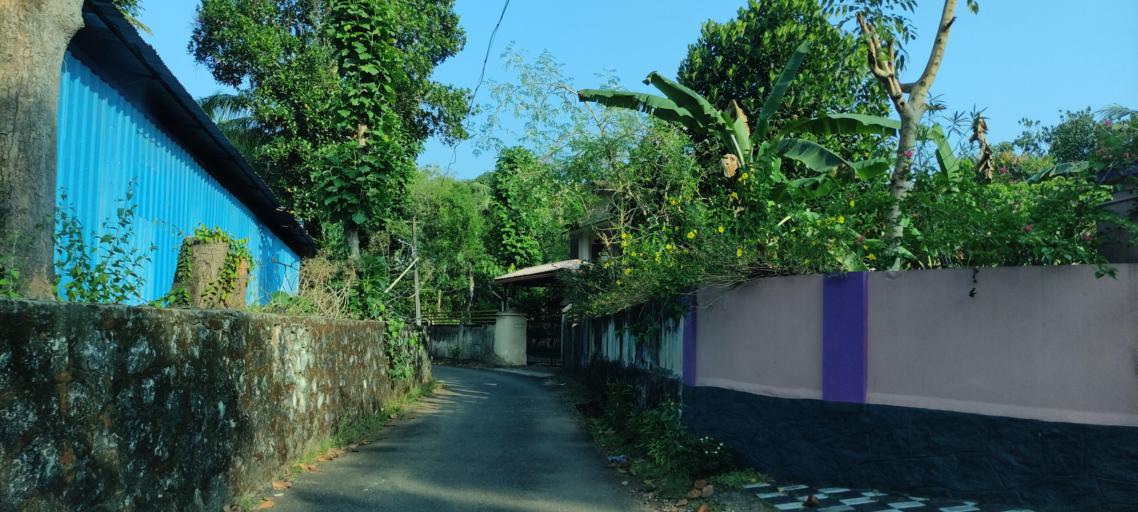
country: IN
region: Kerala
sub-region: Pattanamtitta
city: Adur
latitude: 9.1548
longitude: 76.7396
